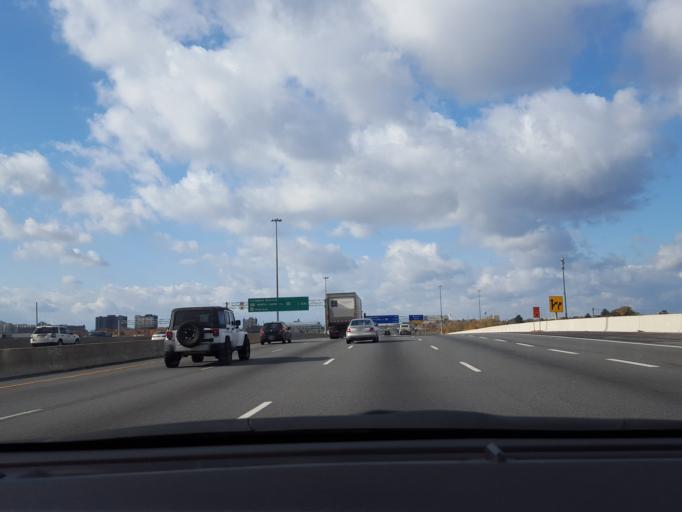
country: CA
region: Ontario
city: Etobicoke
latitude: 43.7153
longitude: -79.5288
